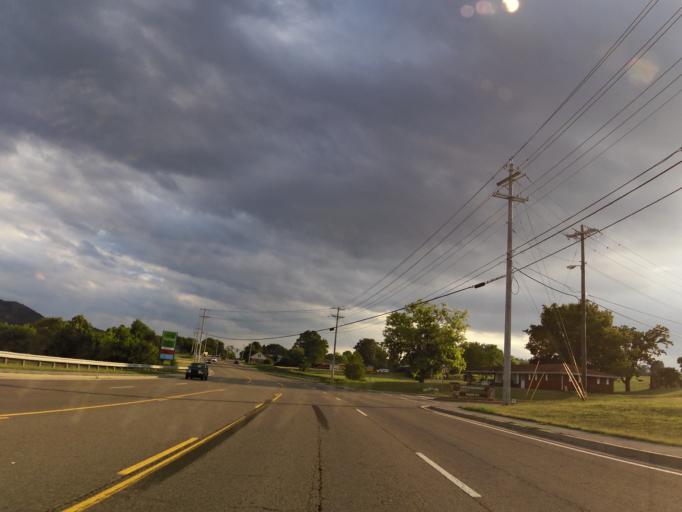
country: US
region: Tennessee
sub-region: Knox County
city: Knoxville
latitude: 36.0617
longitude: -83.9792
